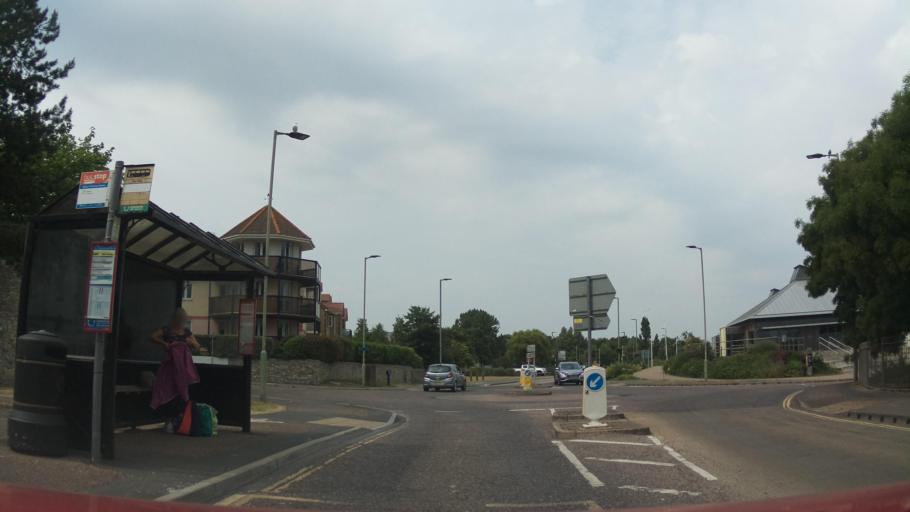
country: GB
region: England
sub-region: Devon
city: Colyton
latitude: 50.7051
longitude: -3.0683
